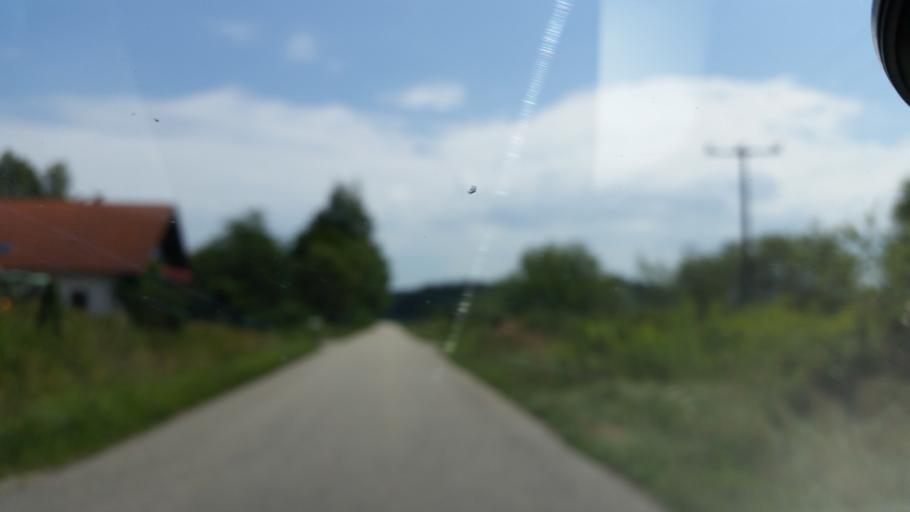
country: DE
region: Bavaria
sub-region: Lower Bavaria
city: Geisenhausen
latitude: 48.4594
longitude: 12.2856
